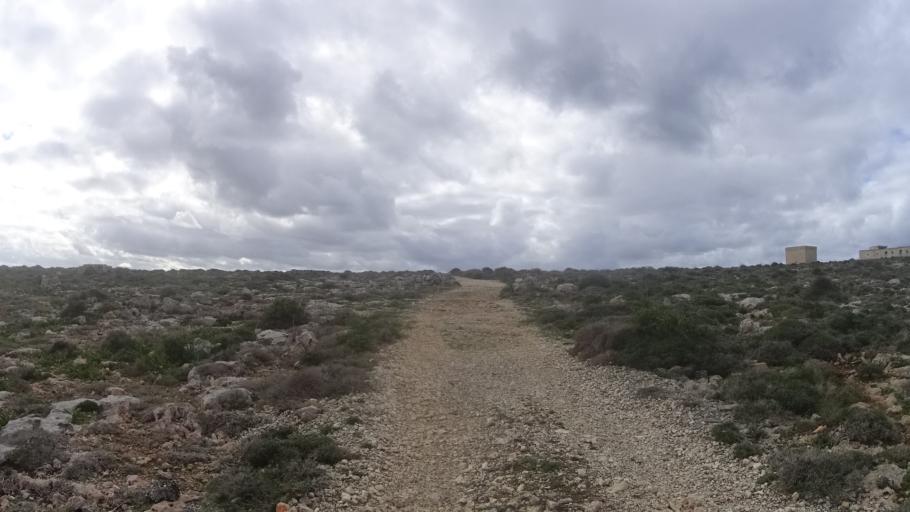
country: MT
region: Il-Mellieha
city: Mellieha
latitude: 35.9731
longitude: 14.3264
